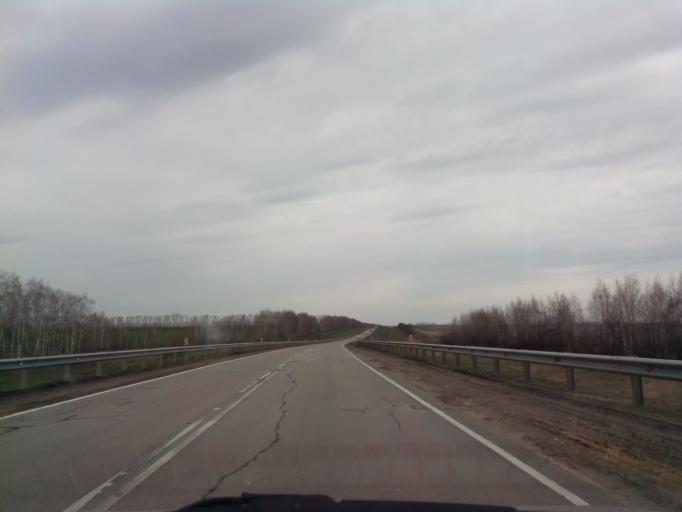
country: RU
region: Tambov
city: Znamenka
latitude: 52.4176
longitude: 41.3771
